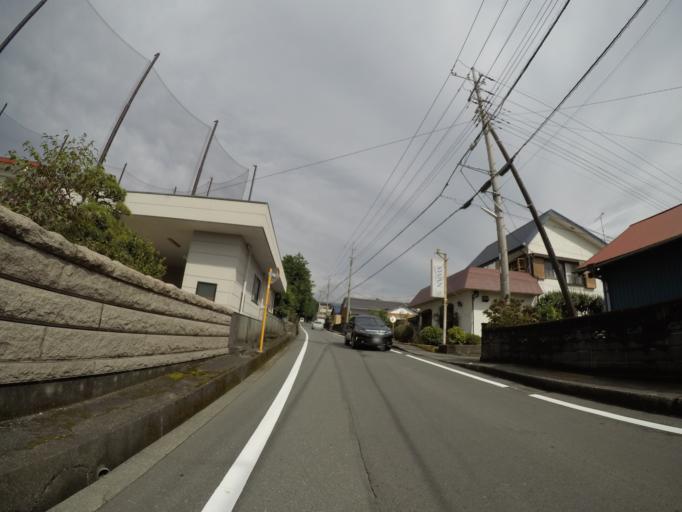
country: JP
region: Shizuoka
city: Fuji
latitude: 35.2069
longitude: 138.6702
